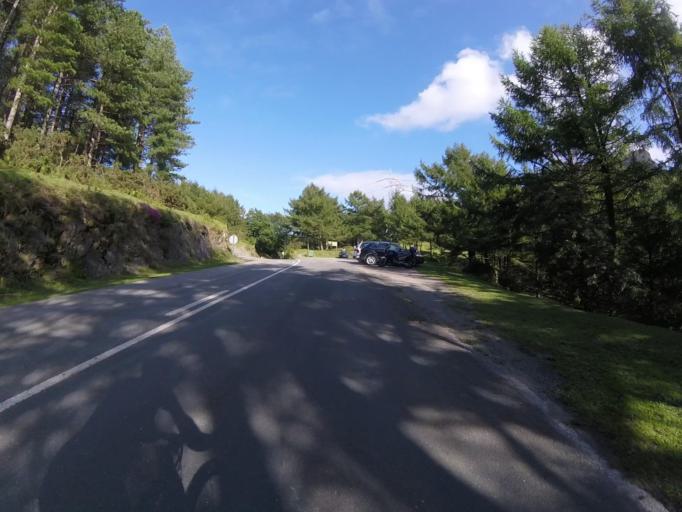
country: ES
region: Basque Country
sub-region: Provincia de Guipuzcoa
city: Irun
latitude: 43.2954
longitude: -1.7871
